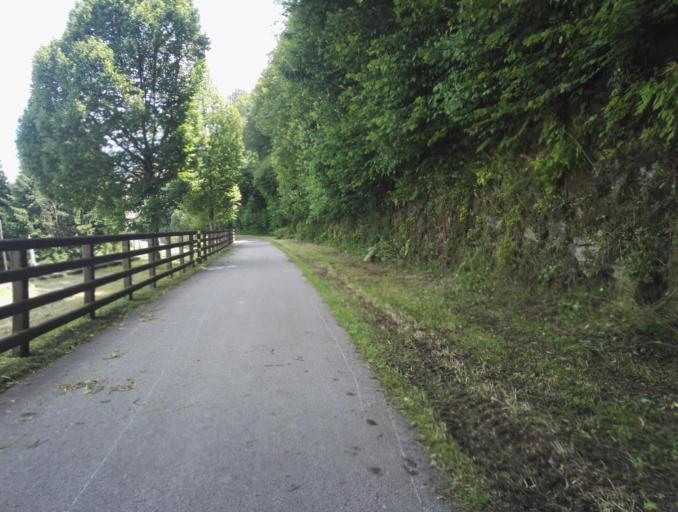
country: AT
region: Styria
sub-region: Politischer Bezirk Graz-Umgebung
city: Gratkorn
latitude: 47.1173
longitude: 15.3583
